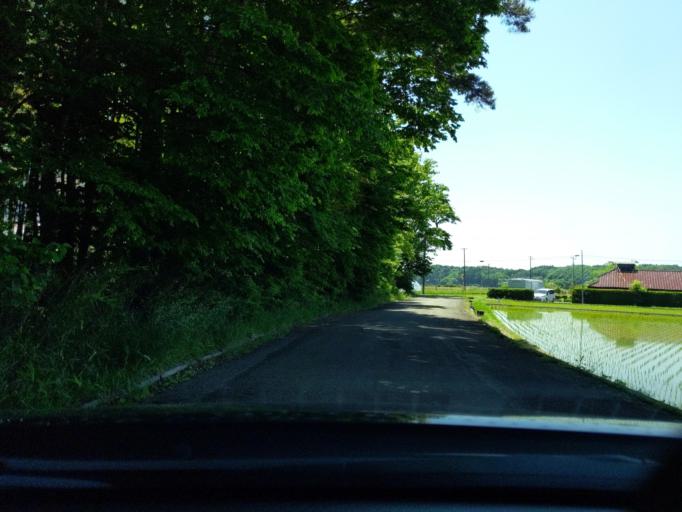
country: JP
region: Fukushima
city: Koriyama
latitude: 37.3885
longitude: 140.2907
